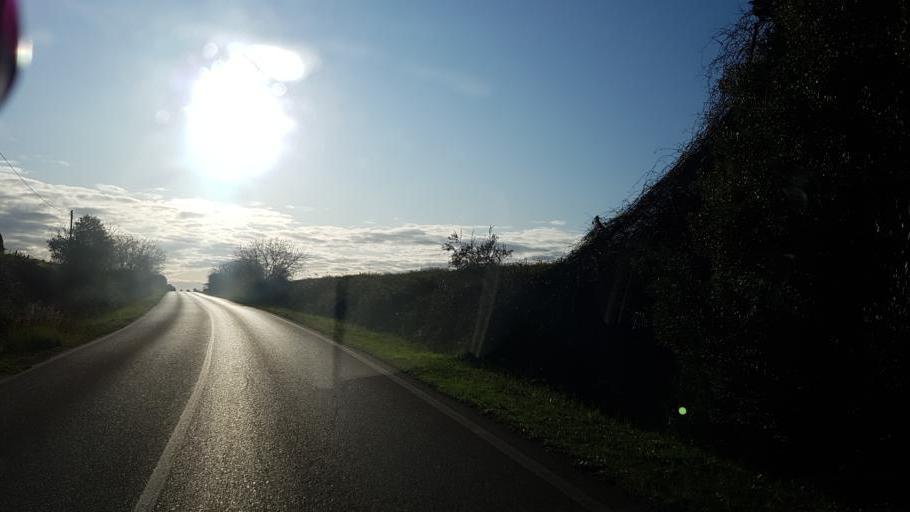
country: IT
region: Apulia
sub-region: Provincia di Brindisi
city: Torchiarolo
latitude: 40.5458
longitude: 18.0445
